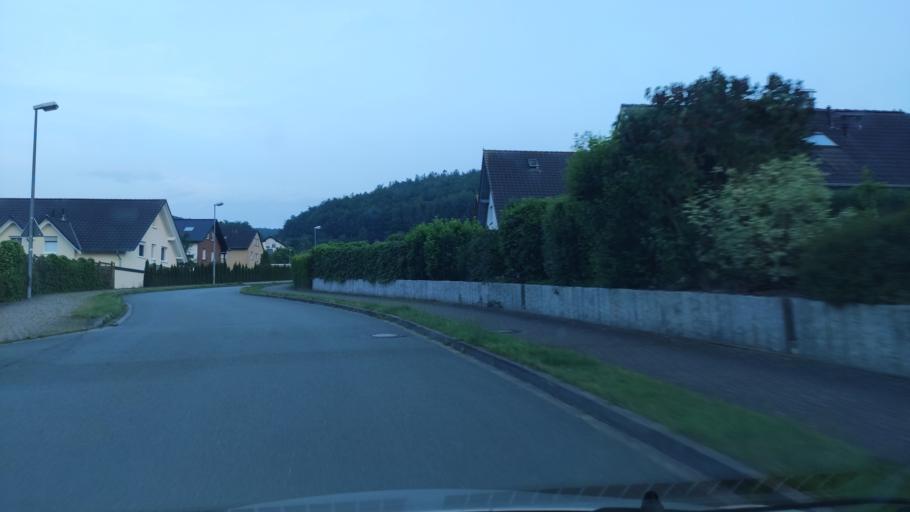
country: DE
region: North Rhine-Westphalia
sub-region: Regierungsbezirk Detmold
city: Hoexter
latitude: 51.7720
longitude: 9.3509
